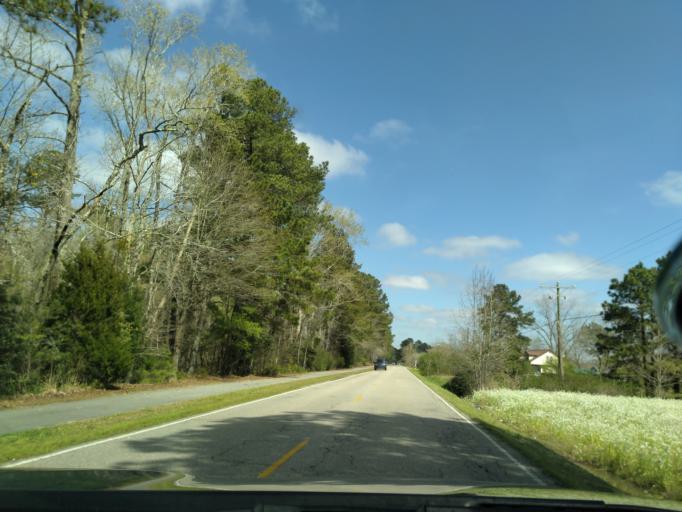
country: US
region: Virginia
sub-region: City of Portsmouth
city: Portsmouth Heights
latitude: 36.7024
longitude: -76.3557
